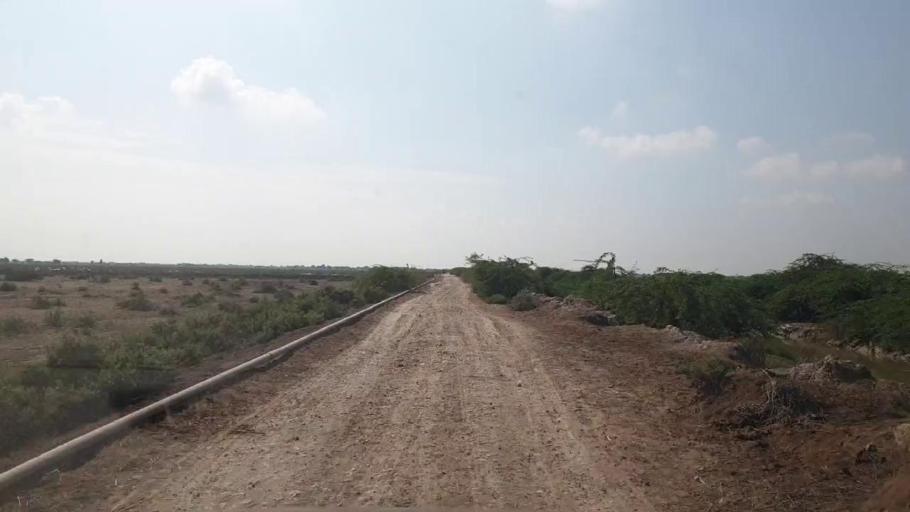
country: PK
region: Sindh
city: Badin
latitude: 24.5023
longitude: 68.6078
